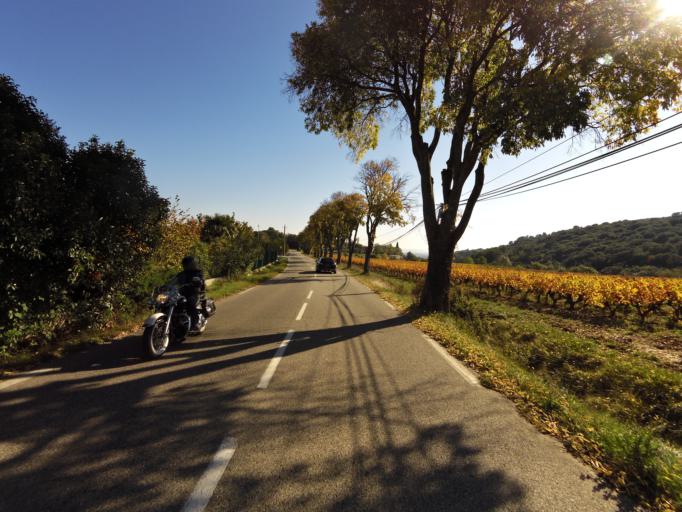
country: FR
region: Rhone-Alpes
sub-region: Departement de l'Ardeche
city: Bourg-Saint-Andeol
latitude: 44.3822
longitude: 4.6299
